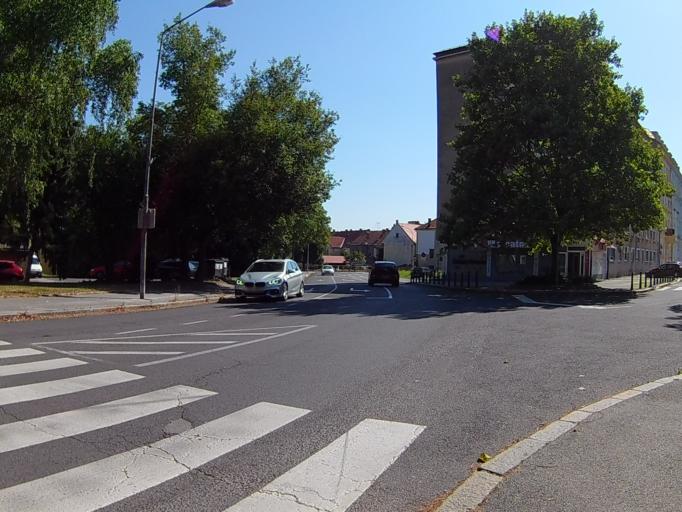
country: SI
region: Maribor
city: Maribor
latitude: 46.5534
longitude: 15.6406
